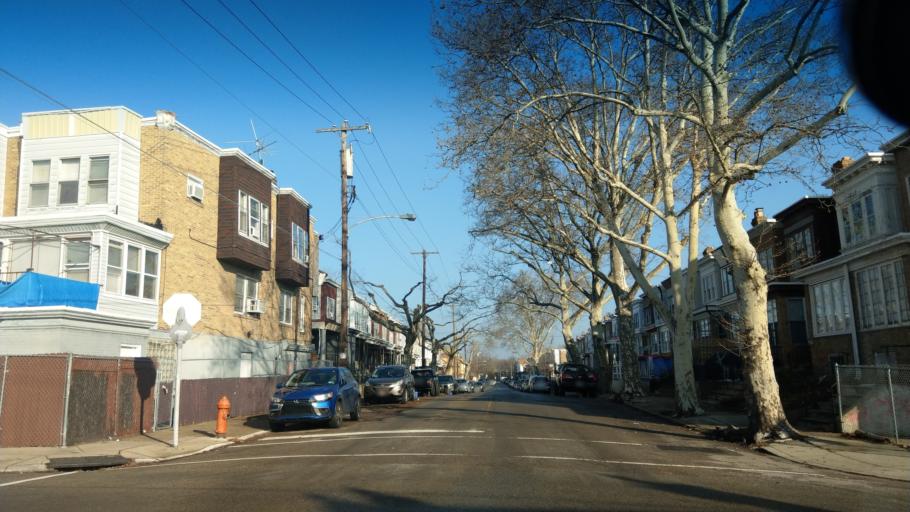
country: US
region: Pennsylvania
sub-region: Montgomery County
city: Rockledge
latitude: 40.0236
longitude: -75.1160
